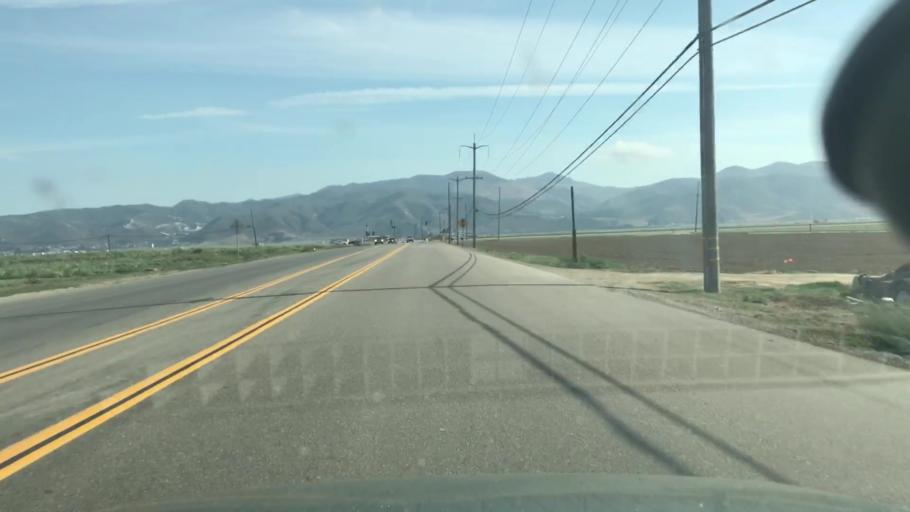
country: US
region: California
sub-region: Santa Barbara County
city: Lompoc
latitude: 34.6641
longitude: -120.4941
